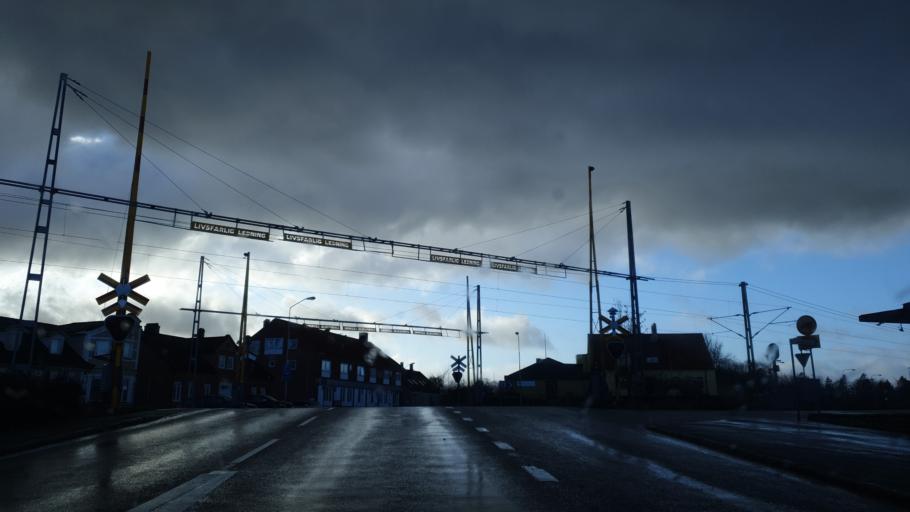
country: SE
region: Skane
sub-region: Skurups Kommun
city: Rydsgard
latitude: 55.4741
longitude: 13.5907
